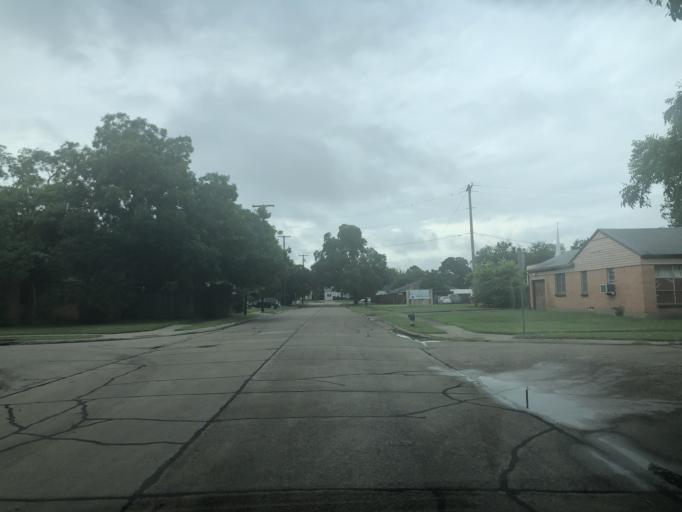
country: US
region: Texas
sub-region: Dallas County
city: Irving
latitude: 32.7996
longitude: -96.9496
